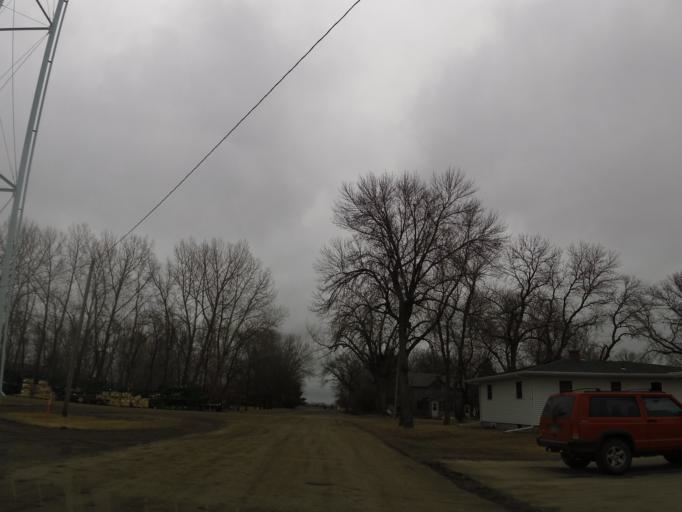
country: US
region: North Dakota
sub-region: Traill County
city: Hillsboro
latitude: 47.1926
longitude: -97.2169
